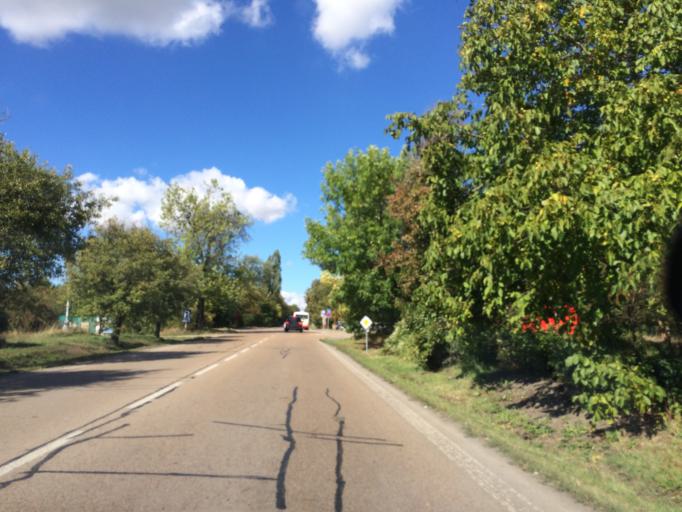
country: CZ
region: Central Bohemia
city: Hostivice
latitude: 50.0850
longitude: 14.3087
